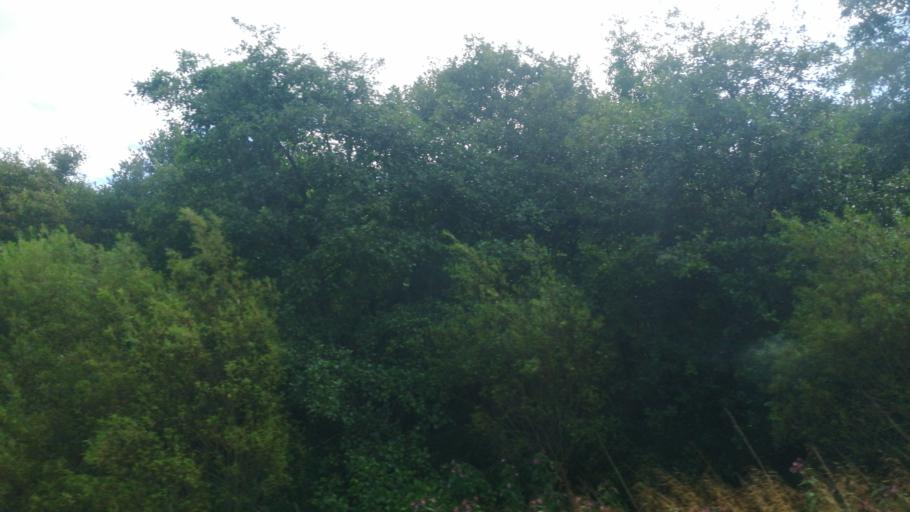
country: GB
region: Scotland
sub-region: Aberdeenshire
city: Insch
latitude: 57.3370
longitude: -2.6377
